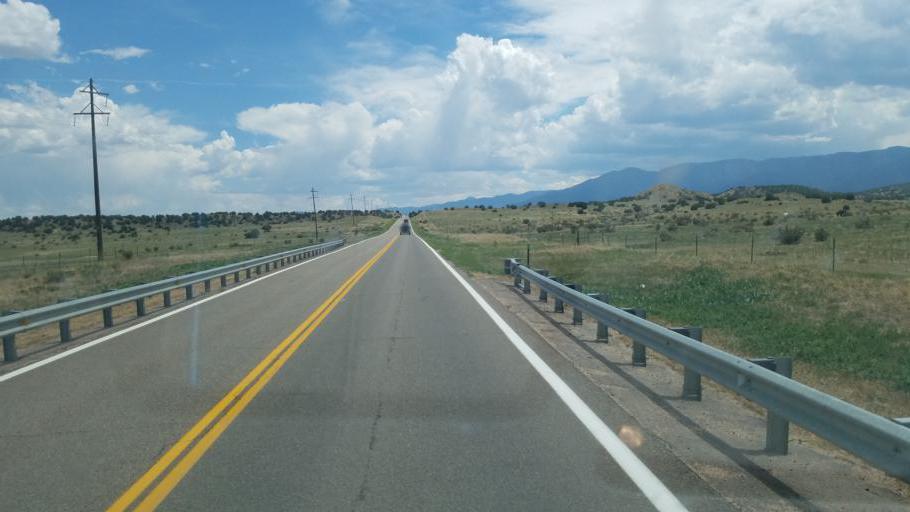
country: US
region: Colorado
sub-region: Fremont County
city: Florence
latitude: 38.3398
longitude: -105.1067
